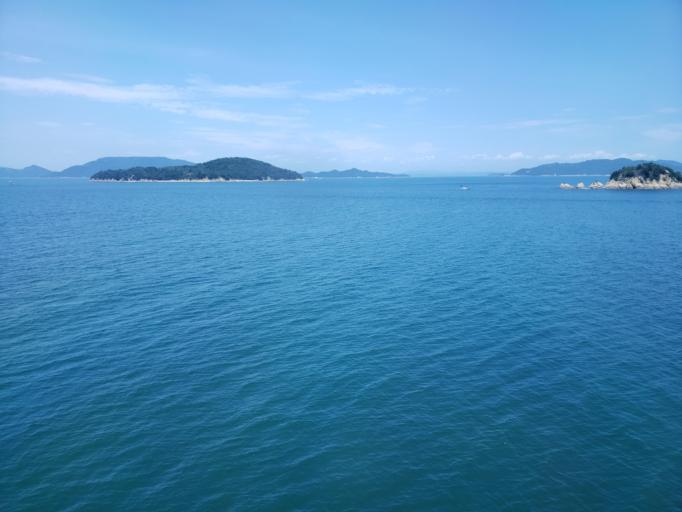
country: JP
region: Kagawa
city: Tonosho
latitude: 34.4047
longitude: 134.1323
